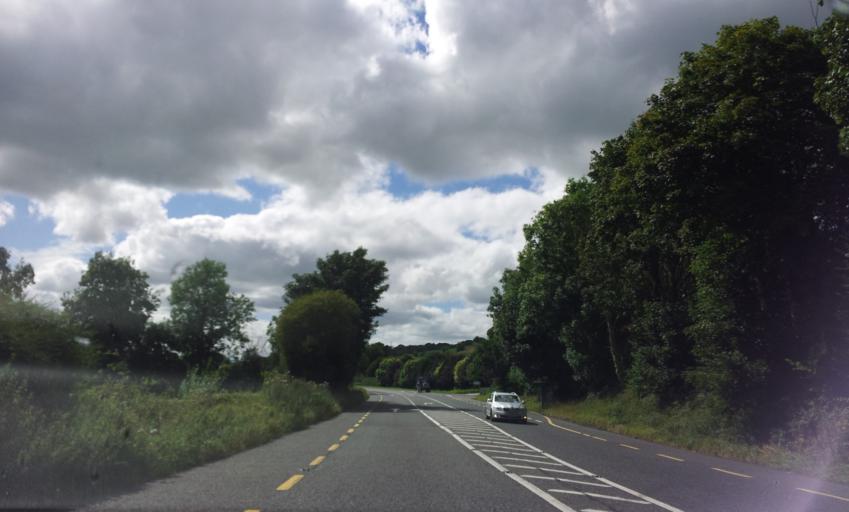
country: IE
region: Munster
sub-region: County Cork
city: Killumney
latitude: 51.8765
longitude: -8.7063
